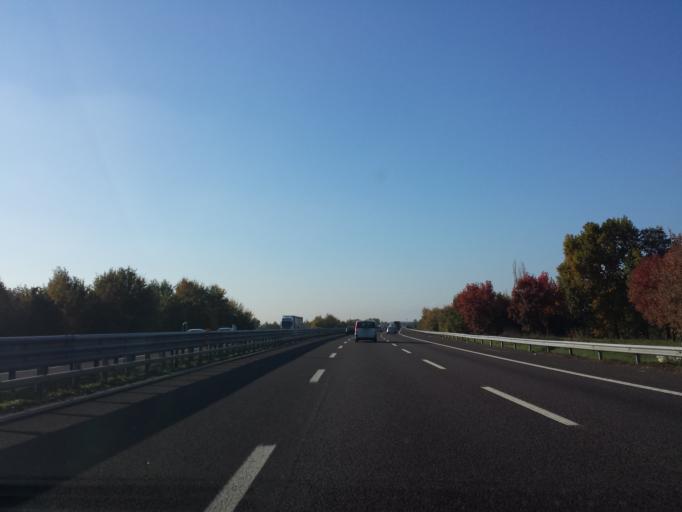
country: IT
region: Veneto
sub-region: Provincia di Padova
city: Bosco
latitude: 45.4563
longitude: 11.7910
